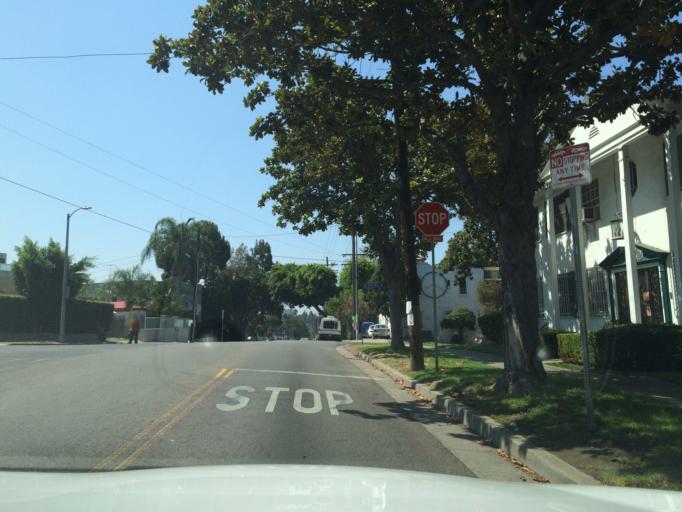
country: US
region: California
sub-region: Los Angeles County
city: Silver Lake
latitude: 34.0850
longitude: -118.2845
